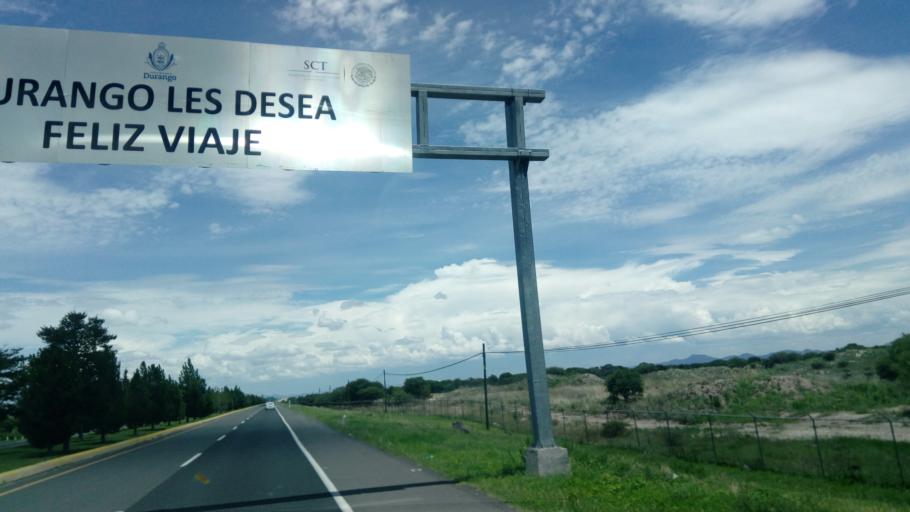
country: MX
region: Durango
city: Victoria de Durango
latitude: 24.1169
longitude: -104.5465
